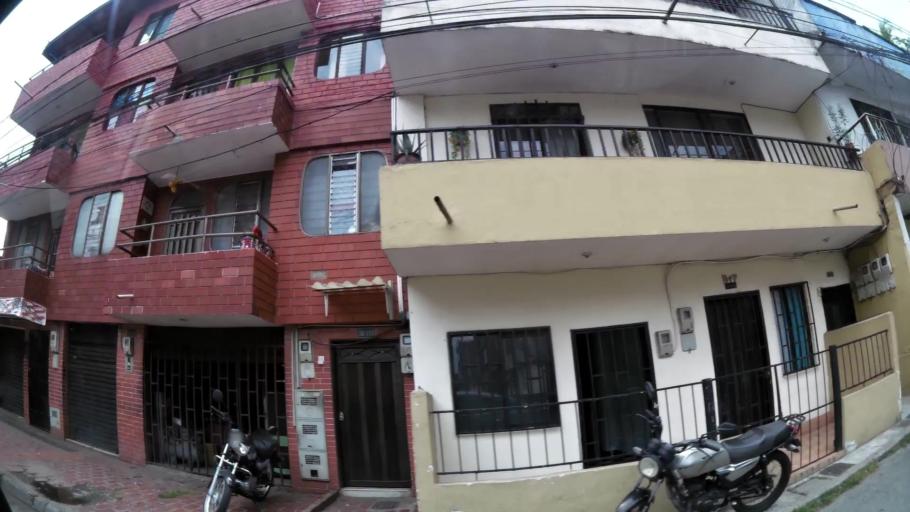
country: CO
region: Antioquia
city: Sabaneta
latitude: 6.1654
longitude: -75.6152
